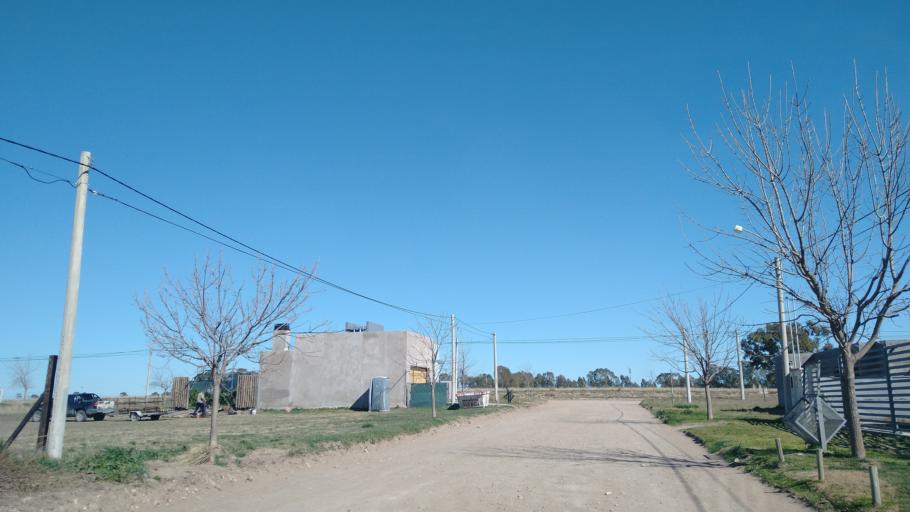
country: AR
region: Buenos Aires
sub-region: Partido de Bahia Blanca
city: Bahia Blanca
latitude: -38.7110
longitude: -62.2035
